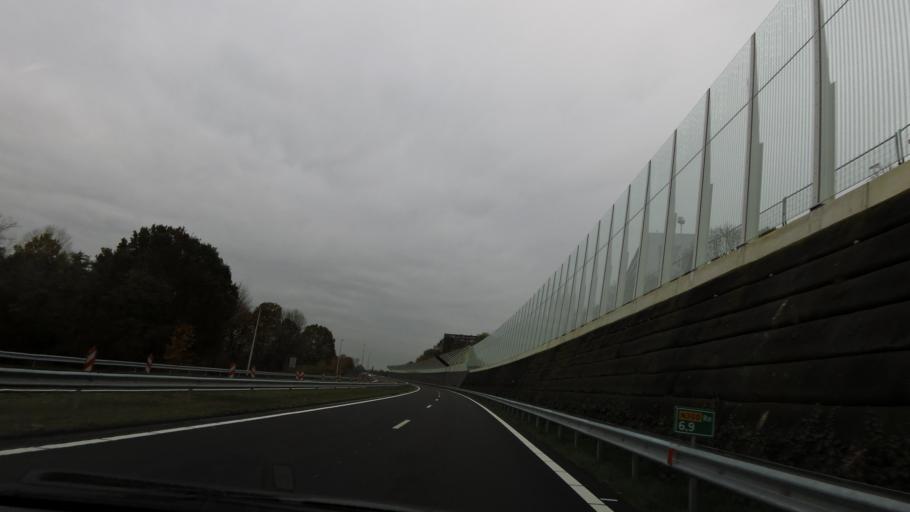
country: NL
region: Limburg
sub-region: Gemeente Onderbanken
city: Merkelbeek
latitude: 50.9482
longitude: 5.9544
